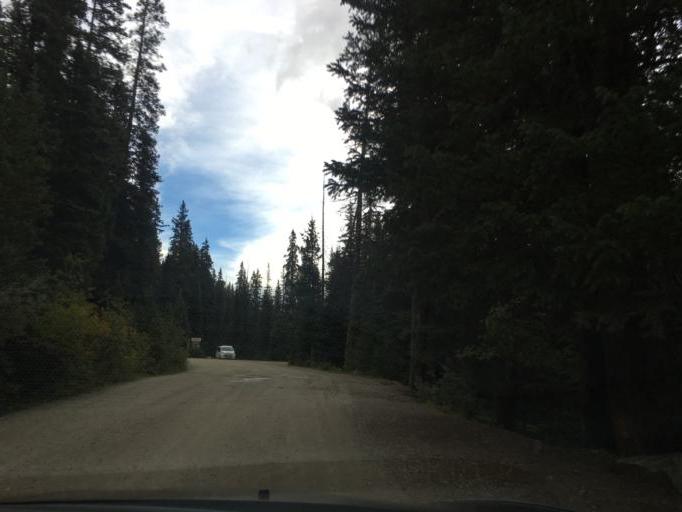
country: US
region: Colorado
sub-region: Summit County
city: Breckenridge
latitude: 39.3844
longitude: -106.0622
